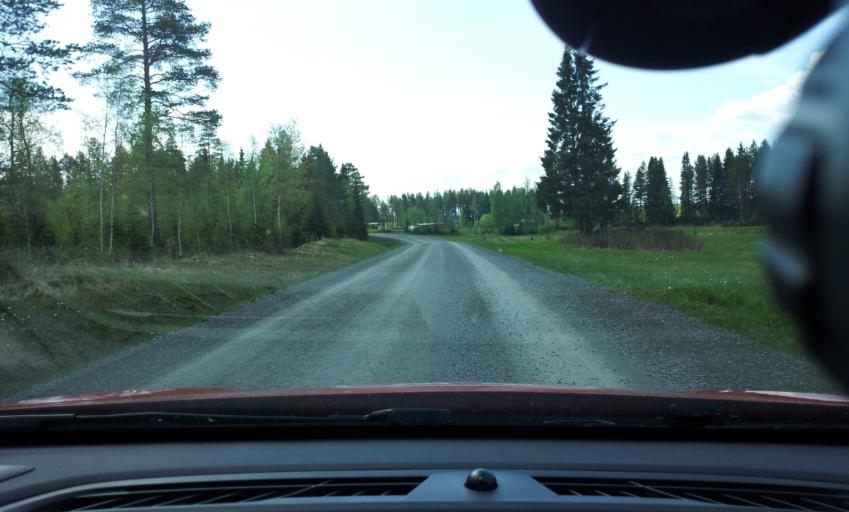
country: SE
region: Jaemtland
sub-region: OEstersunds Kommun
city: Ostersund
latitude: 63.0244
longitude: 14.5845
